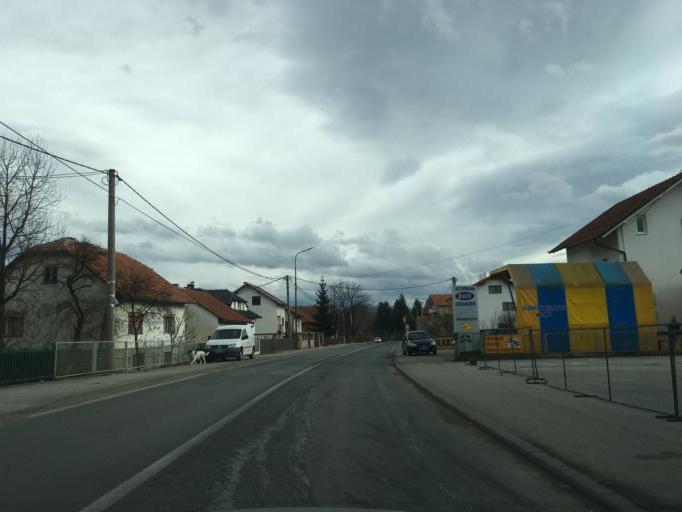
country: BA
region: Federation of Bosnia and Herzegovina
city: Bugojno
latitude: 44.0530
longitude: 17.4333
